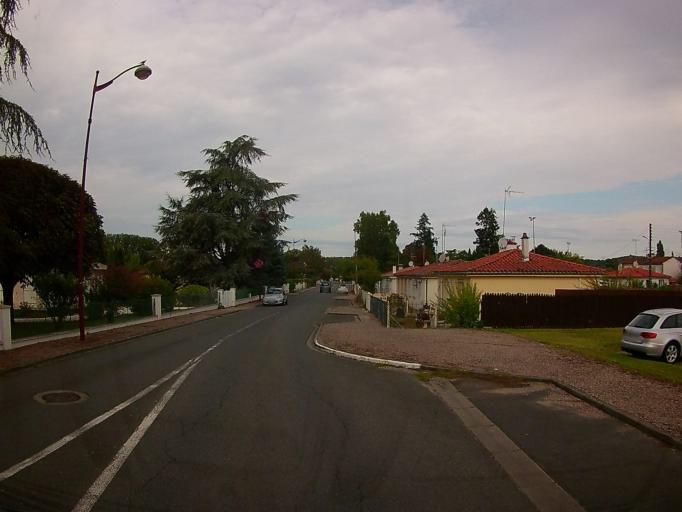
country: FR
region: Aquitaine
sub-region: Departement de la Dordogne
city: Neuvic
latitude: 45.1138
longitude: 0.5027
